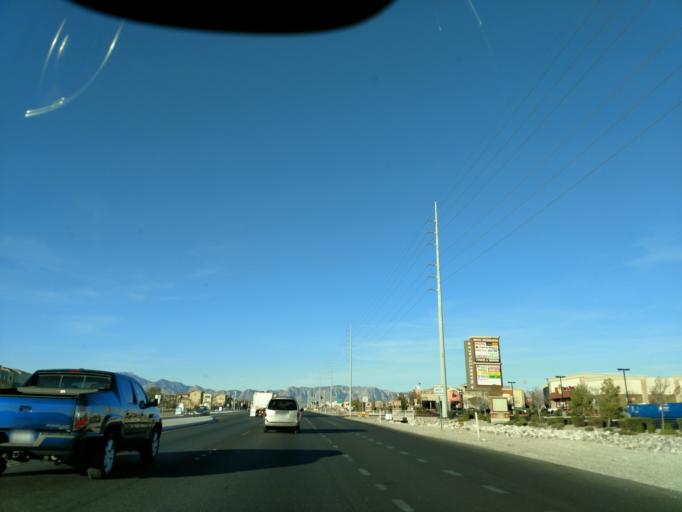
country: US
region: Nevada
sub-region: Clark County
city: Enterprise
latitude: 36.0203
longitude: -115.2672
